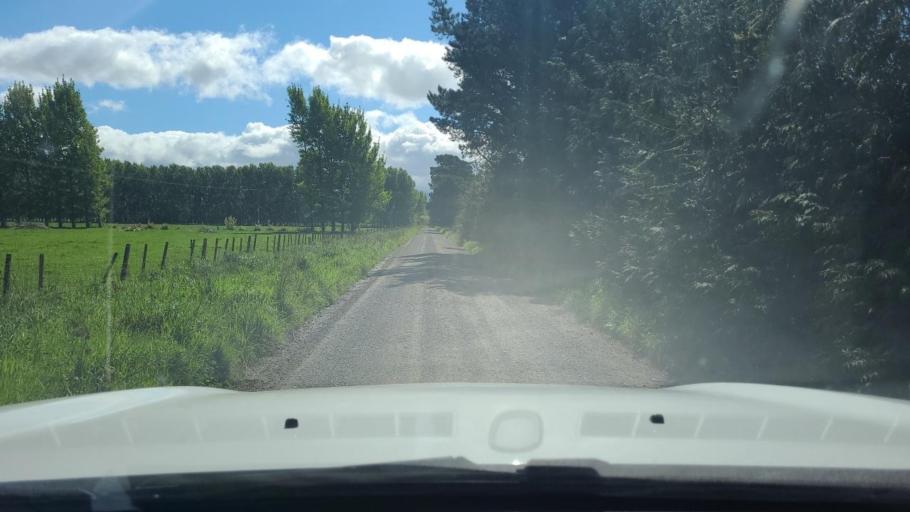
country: NZ
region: Wellington
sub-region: South Wairarapa District
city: Waipawa
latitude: -41.2279
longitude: 175.3194
